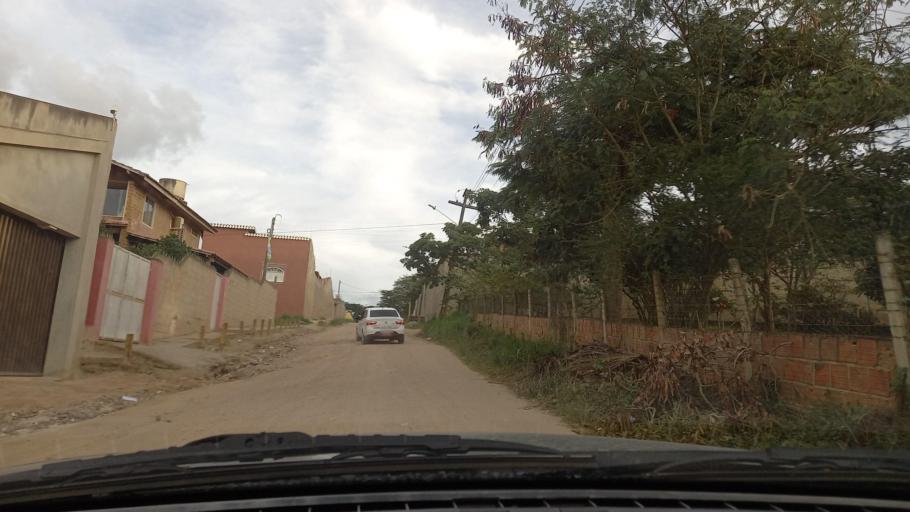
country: BR
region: Pernambuco
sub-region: Gravata
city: Gravata
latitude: -8.1932
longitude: -35.5701
